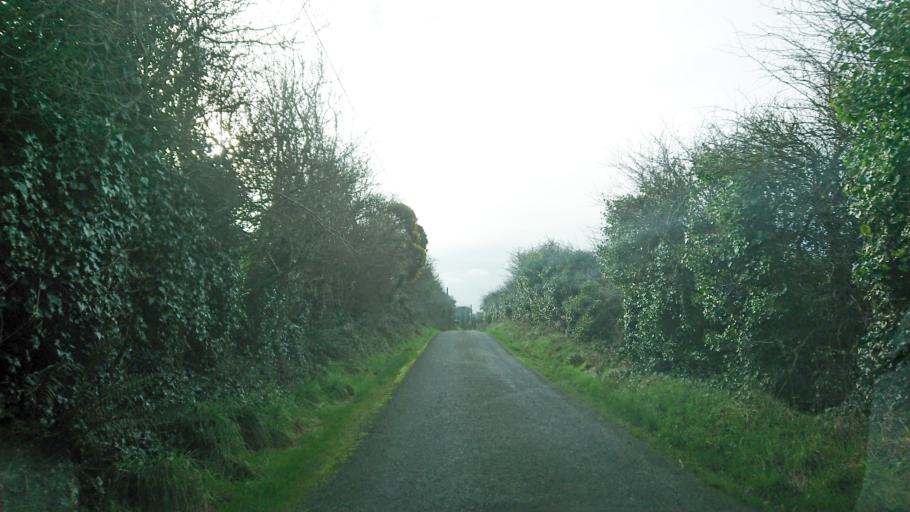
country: IE
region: Munster
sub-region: Waterford
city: Tra Mhor
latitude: 52.1543
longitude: -7.1911
